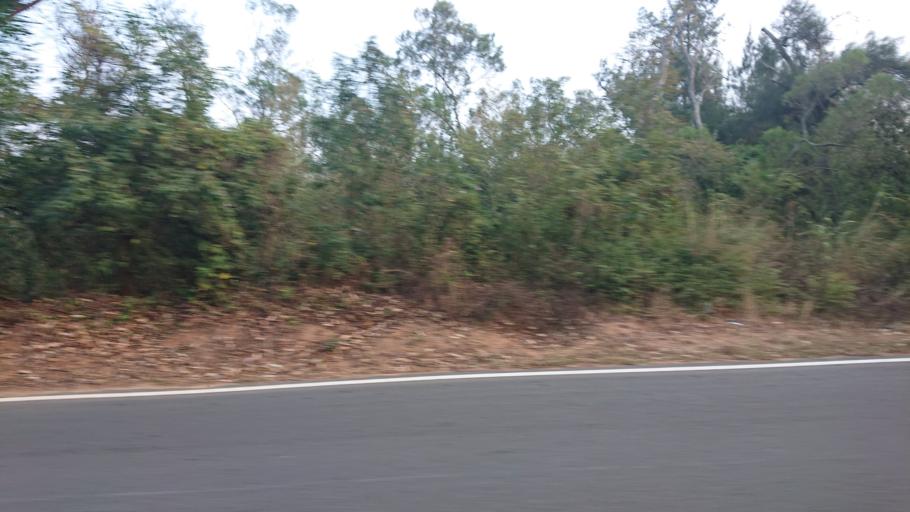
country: CN
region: Fujian
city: Dadeng
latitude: 24.4838
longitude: 118.4380
